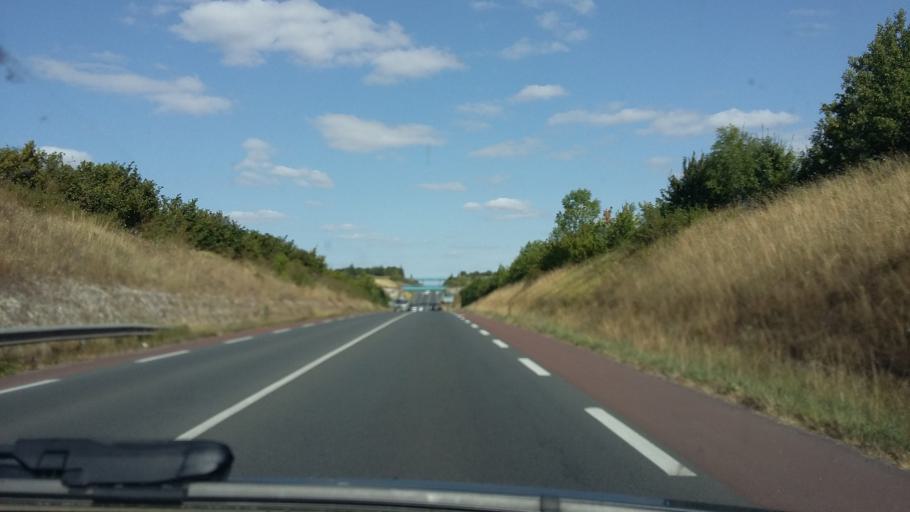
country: FR
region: Poitou-Charentes
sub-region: Departement de la Charente-Maritime
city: Saint-Jean-d'Angely
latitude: 45.9562
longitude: -0.5246
